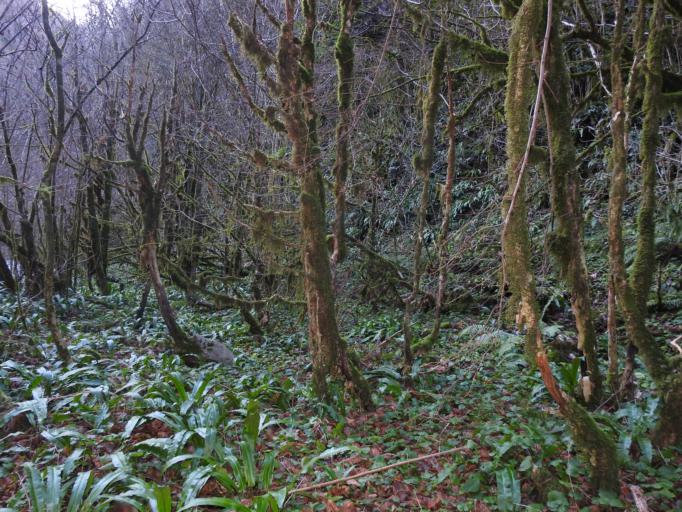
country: GE
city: Gantiadi
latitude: 43.4142
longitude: 40.2162
